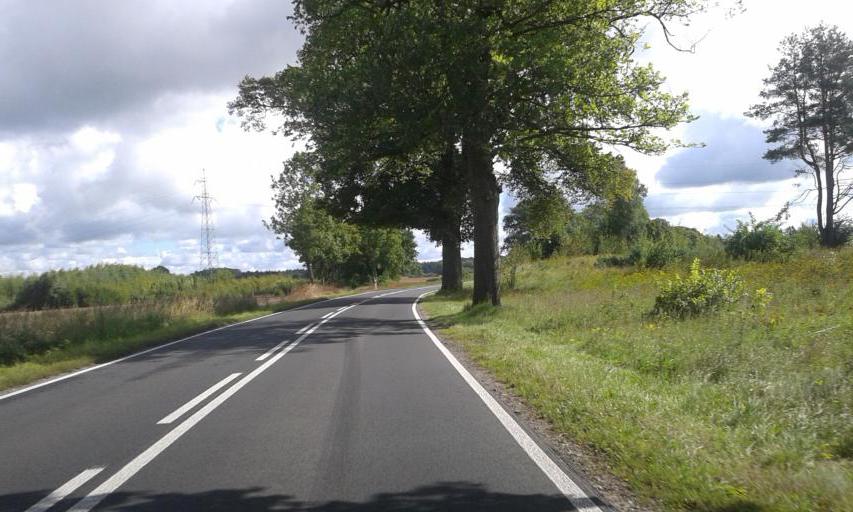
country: PL
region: West Pomeranian Voivodeship
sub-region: Powiat koszalinski
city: Bobolice
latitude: 53.9633
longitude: 16.6077
